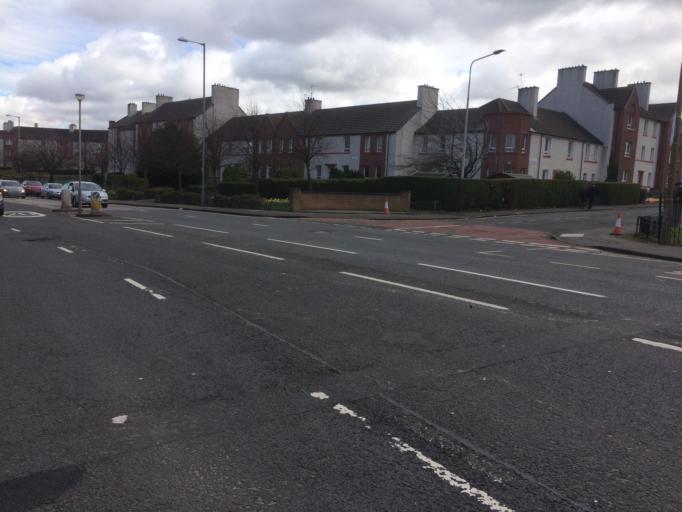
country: GB
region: Scotland
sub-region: West Lothian
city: Seafield
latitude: 55.9320
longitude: -3.1458
